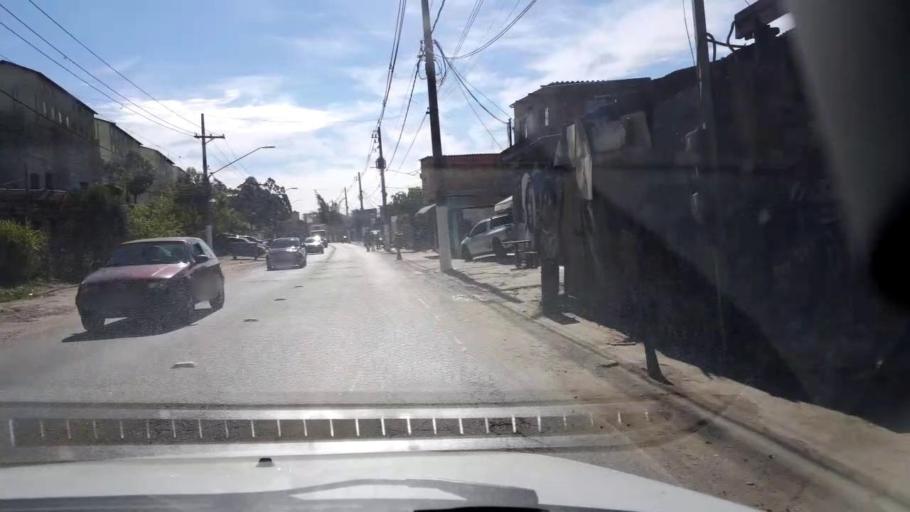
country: BR
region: Sao Paulo
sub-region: Ferraz De Vasconcelos
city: Ferraz de Vasconcelos
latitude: -23.5715
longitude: -46.4155
